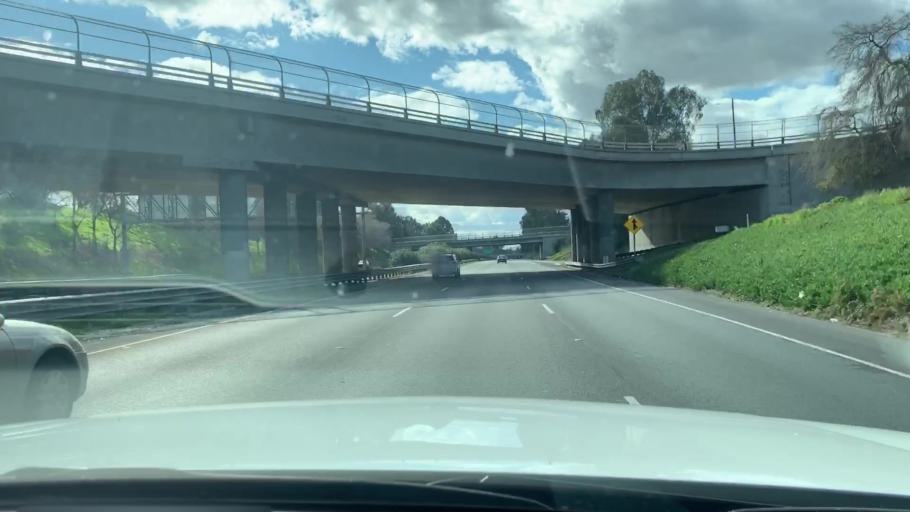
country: US
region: California
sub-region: Kern County
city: Bakersfield
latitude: 35.3859
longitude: -118.9873
